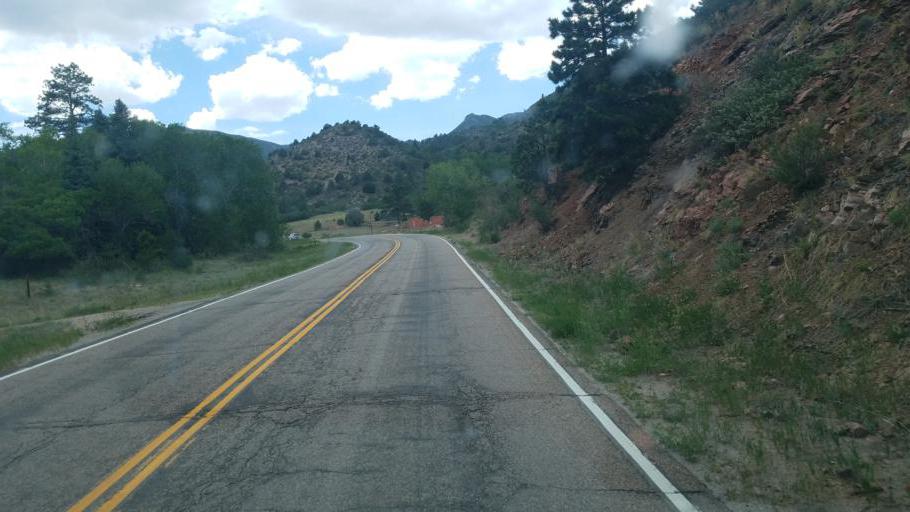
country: US
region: Colorado
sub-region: Fremont County
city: Florence
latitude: 38.1758
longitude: -105.1315
